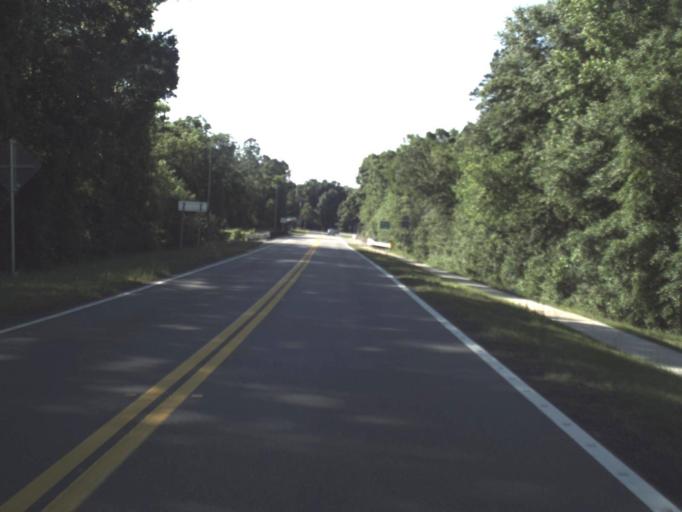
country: US
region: Florida
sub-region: Gulf County
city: Wewahitchka
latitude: 30.0250
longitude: -84.9809
